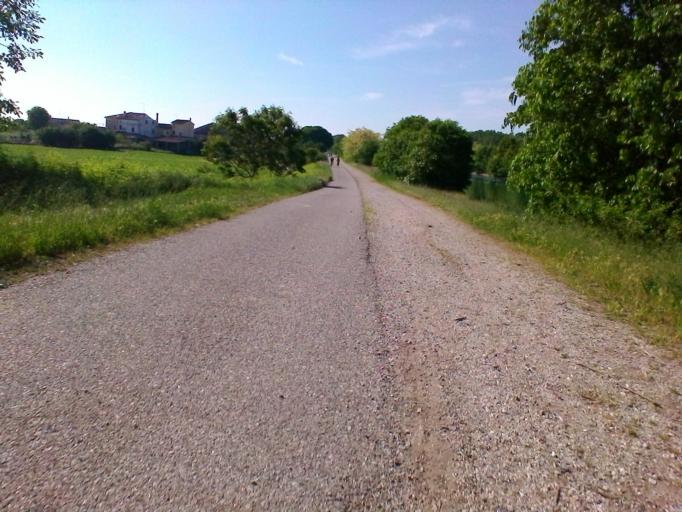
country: IT
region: Lombardy
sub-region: Provincia di Mantova
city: Roverbella
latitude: 45.2675
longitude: 10.7286
